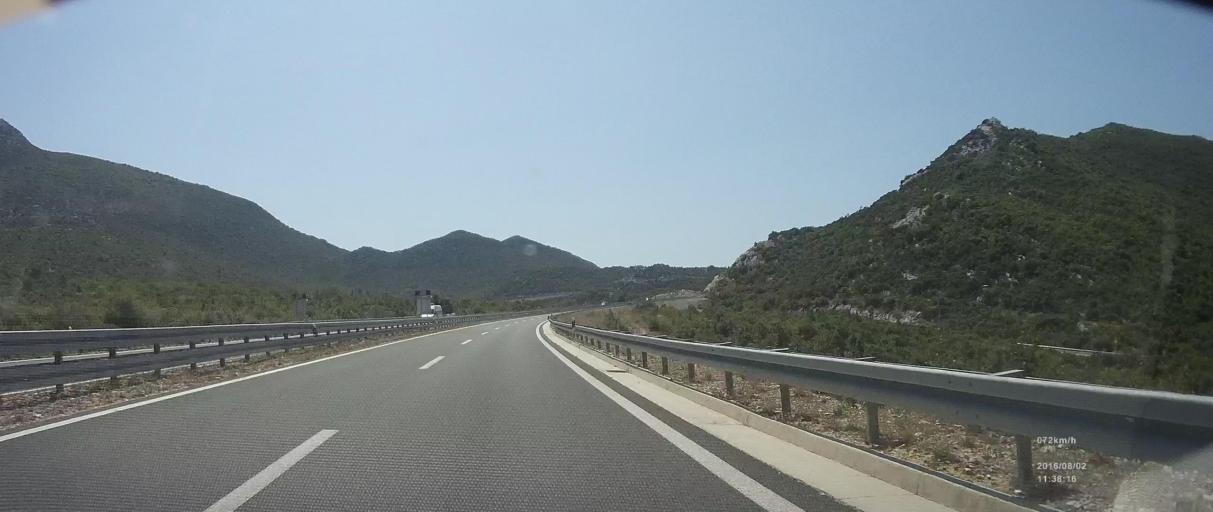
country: HR
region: Dubrovacko-Neretvanska
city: Komin
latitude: 43.0979
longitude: 17.4898
